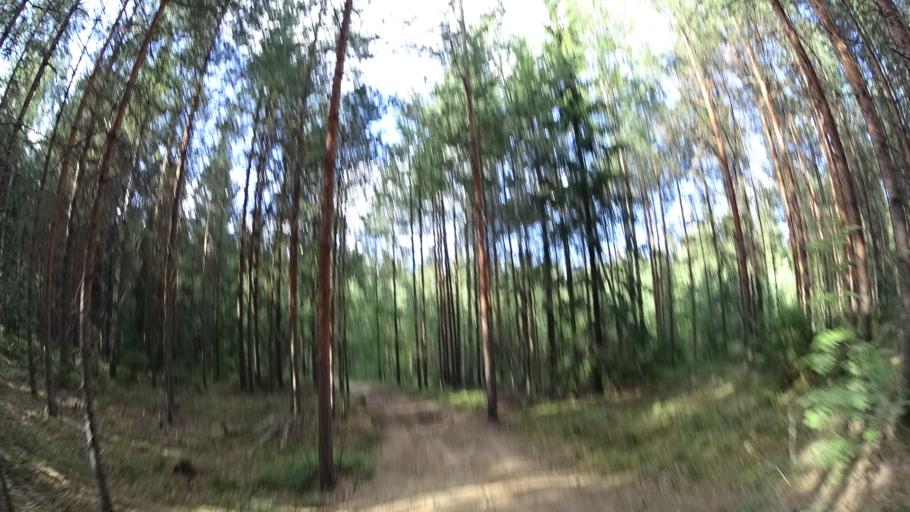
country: FI
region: Uusimaa
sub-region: Helsinki
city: Vihti
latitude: 60.3658
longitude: 24.3538
